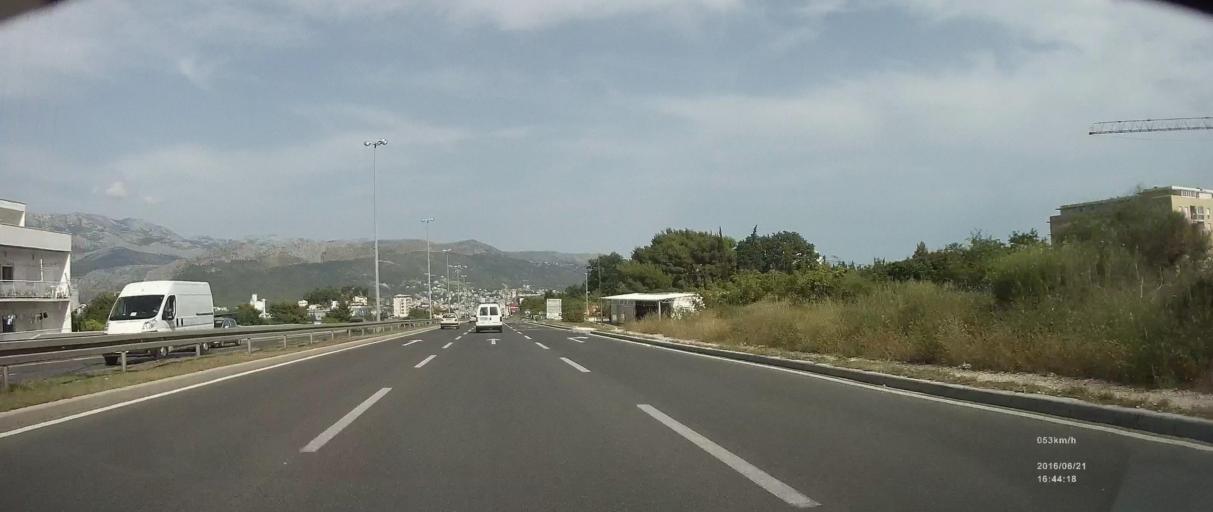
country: HR
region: Splitsko-Dalmatinska
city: Kamen
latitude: 43.5090
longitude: 16.4950
